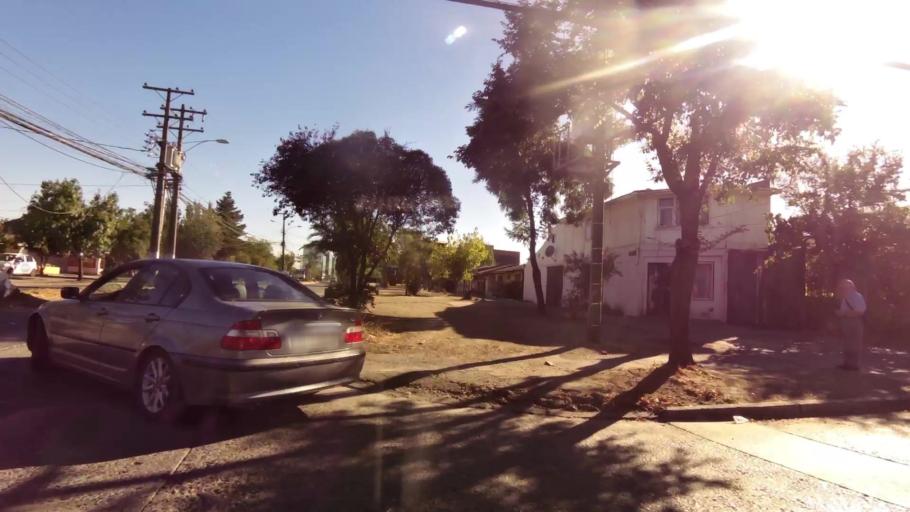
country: CL
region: O'Higgins
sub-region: Provincia de Cachapoal
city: Rancagua
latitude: -34.1835
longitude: -70.7311
